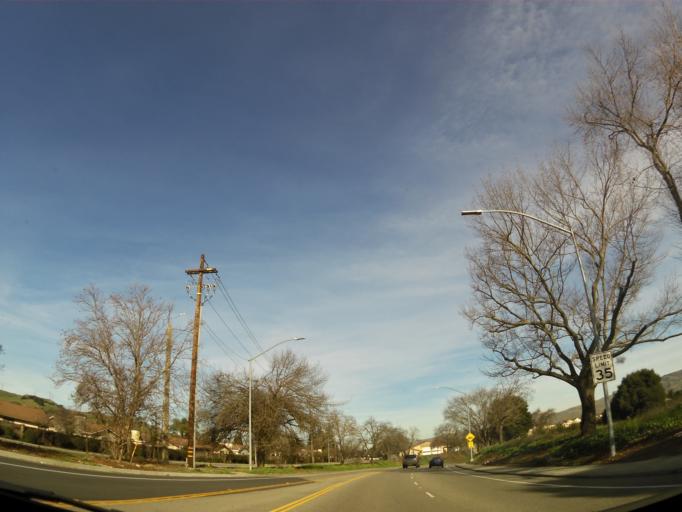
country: US
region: California
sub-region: Santa Clara County
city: Morgan Hill
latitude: 37.1393
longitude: -121.6619
